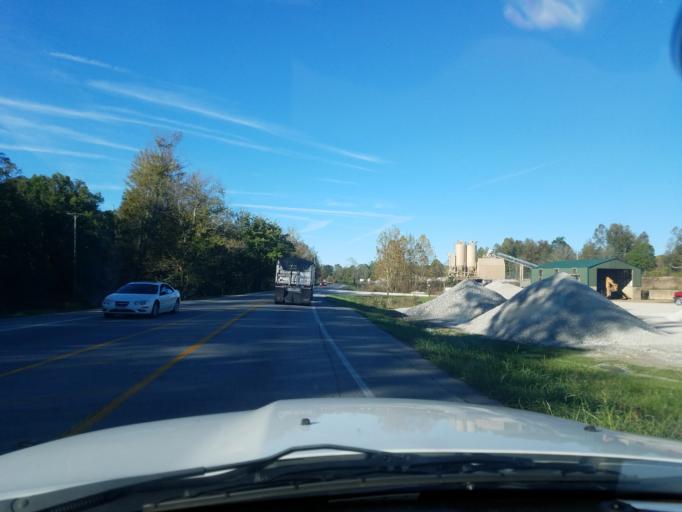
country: US
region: Kentucky
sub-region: Laurel County
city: London
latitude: 37.0686
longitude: -84.0590
